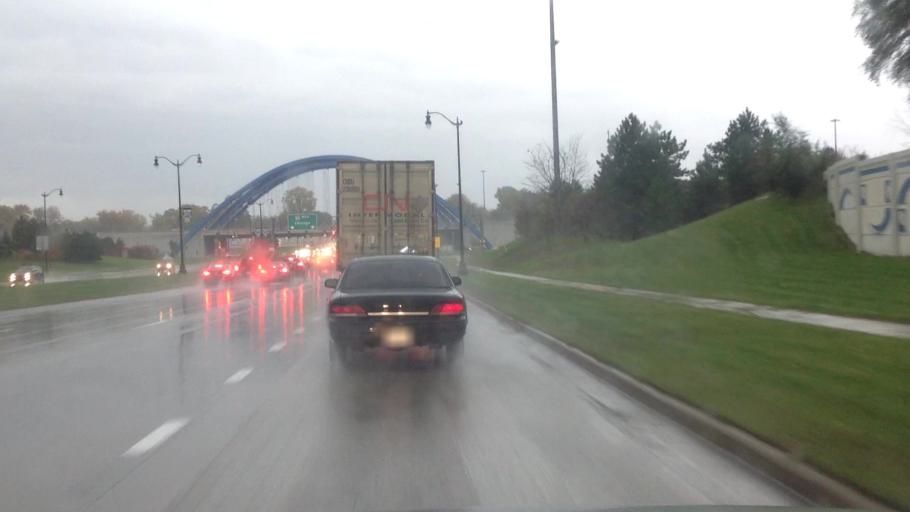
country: US
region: Michigan
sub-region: Wayne County
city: Taylor
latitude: 42.2616
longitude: -83.2702
